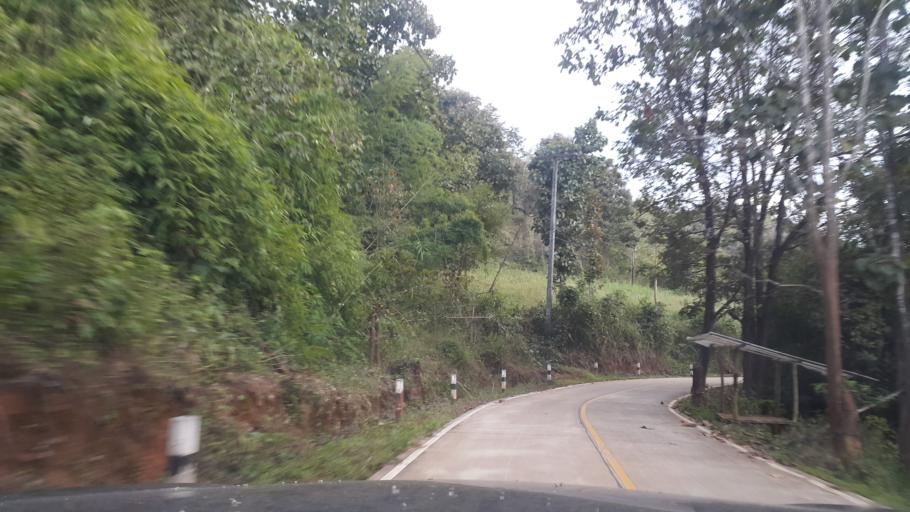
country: TH
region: Chiang Mai
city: Samoeng
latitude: 18.9927
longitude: 98.6747
